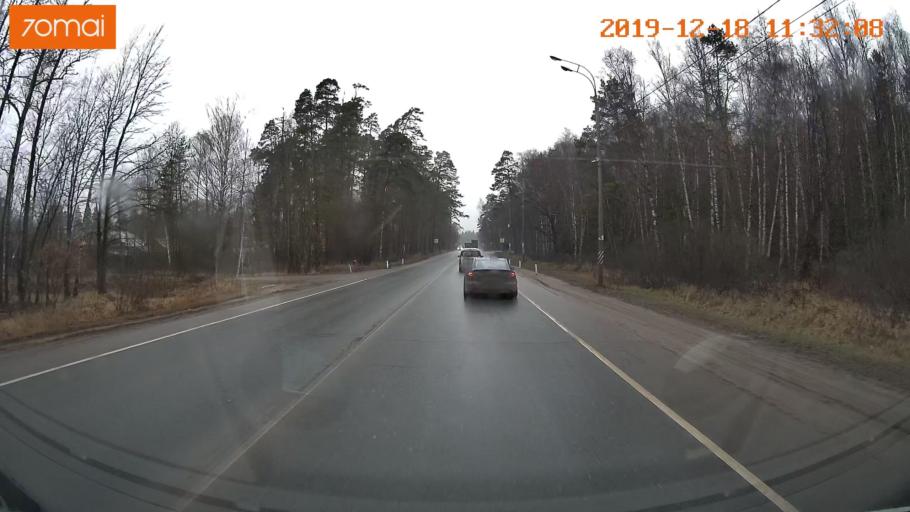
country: RU
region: Moskovskaya
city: Bol'shiye Vyazemy
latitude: 55.6682
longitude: 36.9570
